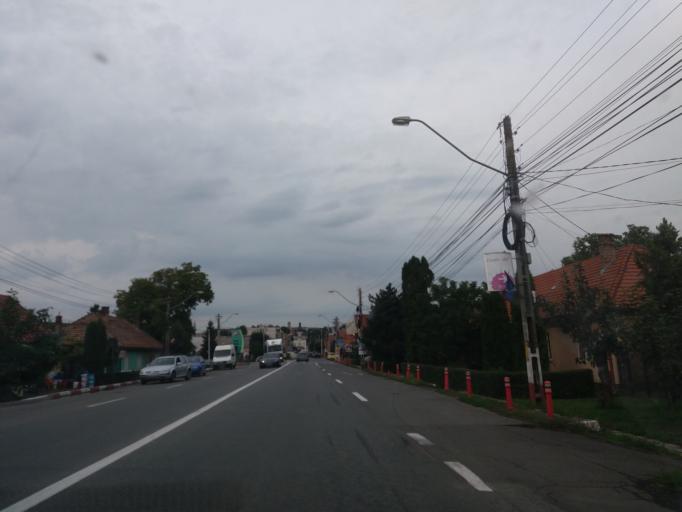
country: RO
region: Mures
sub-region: Municipiul Reghin
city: Reghin
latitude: 46.7698
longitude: 24.7037
